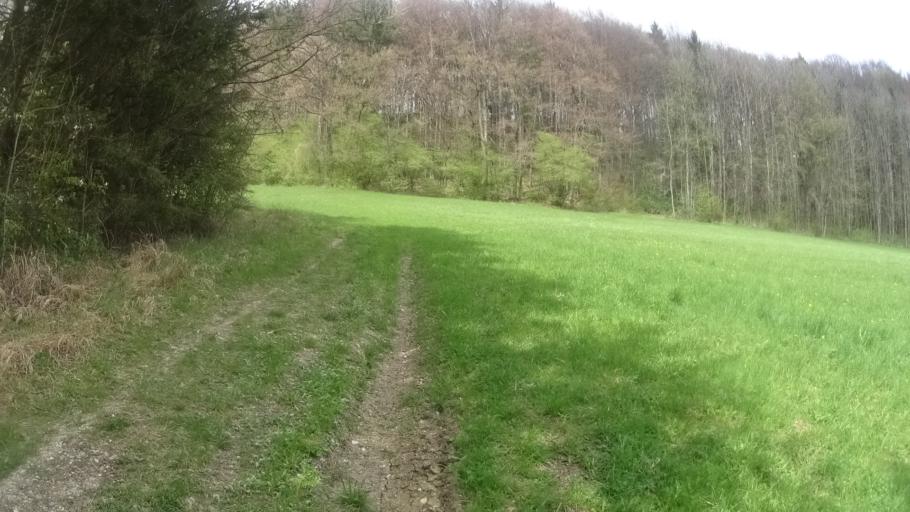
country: DE
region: Bavaria
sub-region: Upper Franconia
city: Kleinsendelbach
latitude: 49.6243
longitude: 11.1828
